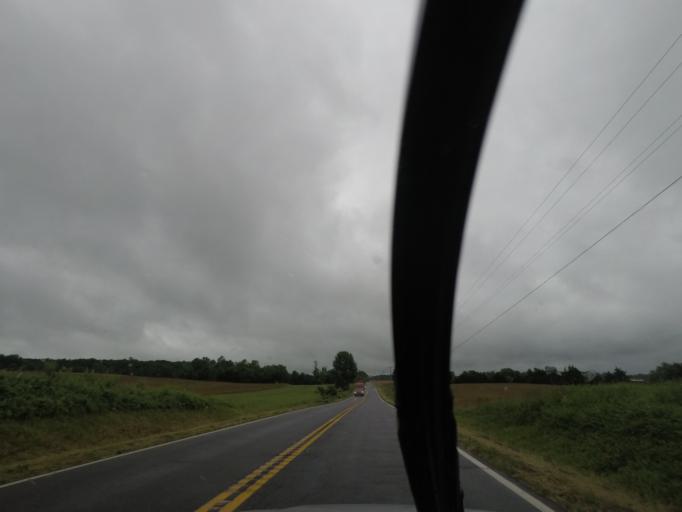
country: US
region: Virginia
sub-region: Culpeper County
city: Merrimac
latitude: 38.4032
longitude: -78.0658
